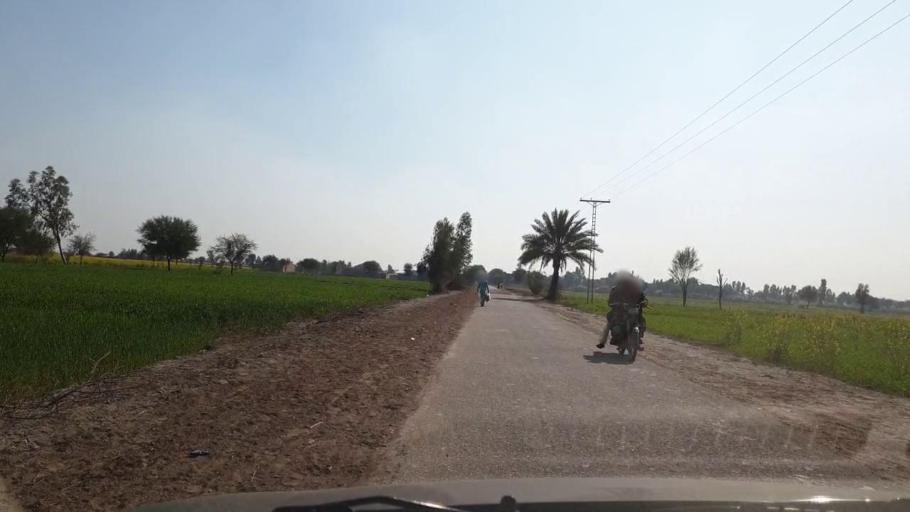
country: PK
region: Sindh
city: Jhol
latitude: 25.9484
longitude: 68.8866
